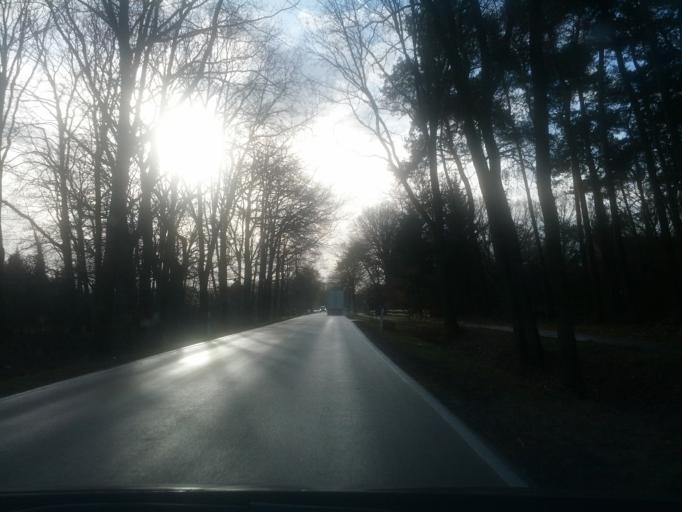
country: DE
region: Lower Saxony
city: Helvesiek
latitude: 53.2222
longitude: 9.4838
